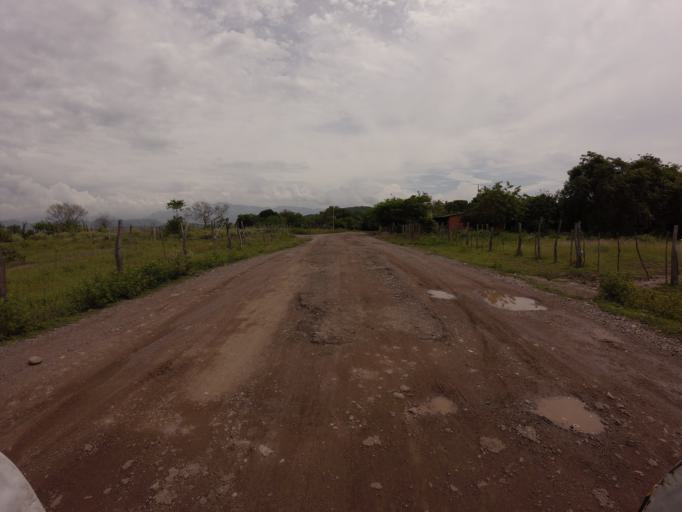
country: CO
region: Tolima
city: Natagaima
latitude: 3.4630
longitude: -75.1405
